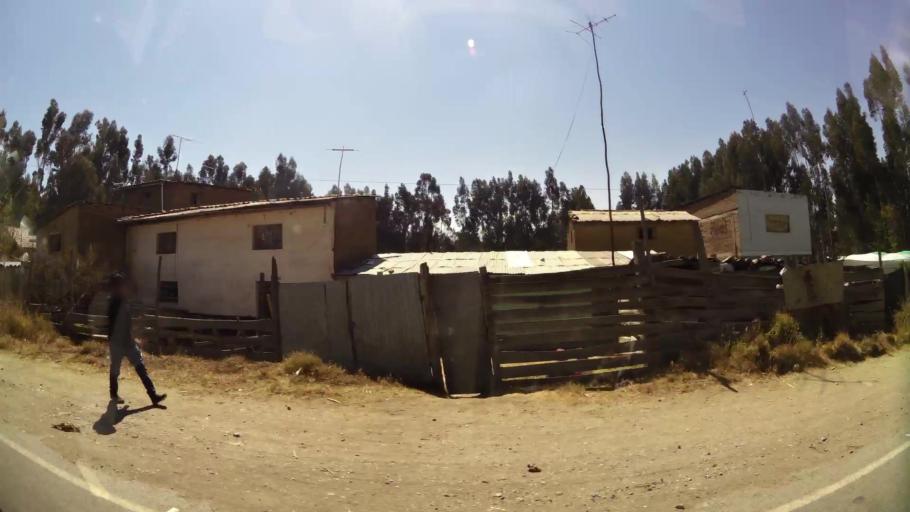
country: PE
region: Junin
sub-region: Provincia de Concepcion
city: Concepcion
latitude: -11.9128
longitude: -75.3265
